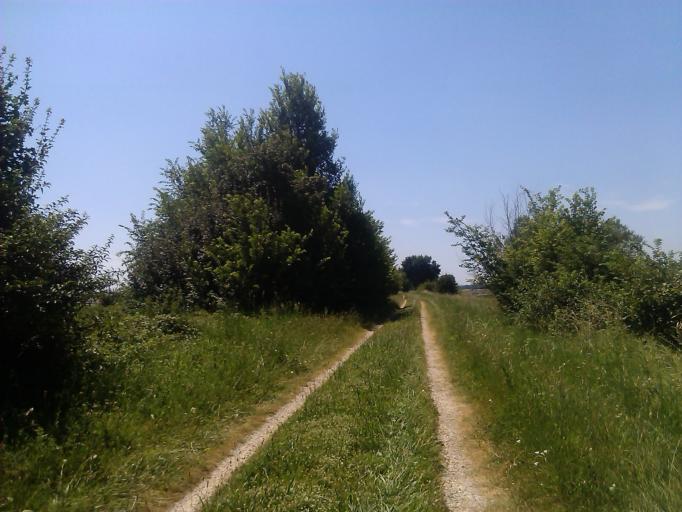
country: IT
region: Tuscany
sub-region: Province of Arezzo
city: Cesa
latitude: 43.3353
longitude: 11.8296
